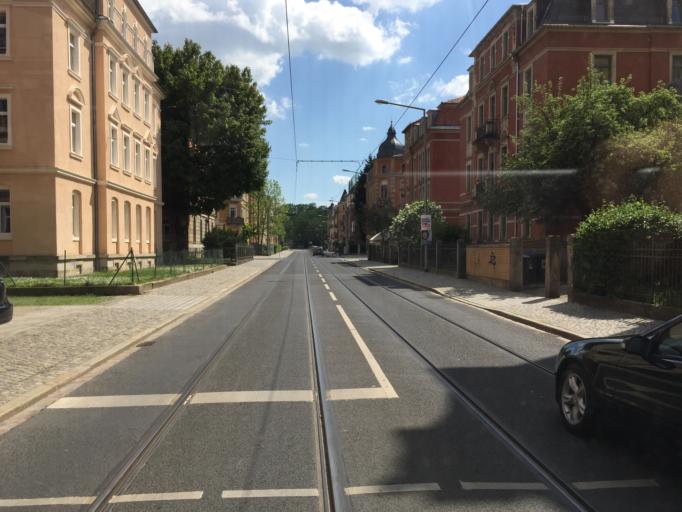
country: DE
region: Saxony
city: Dresden
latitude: 51.0454
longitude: 13.6934
